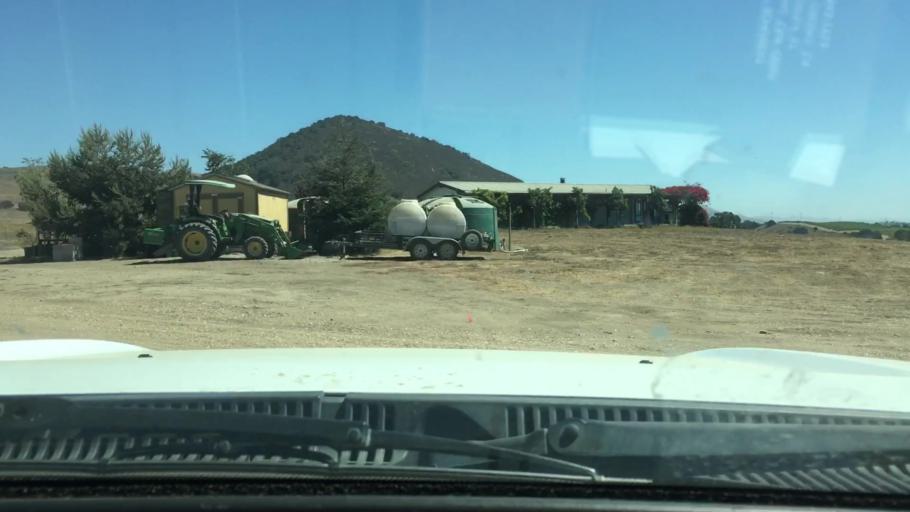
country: US
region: California
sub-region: San Luis Obispo County
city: Arroyo Grande
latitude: 35.1044
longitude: -120.5554
